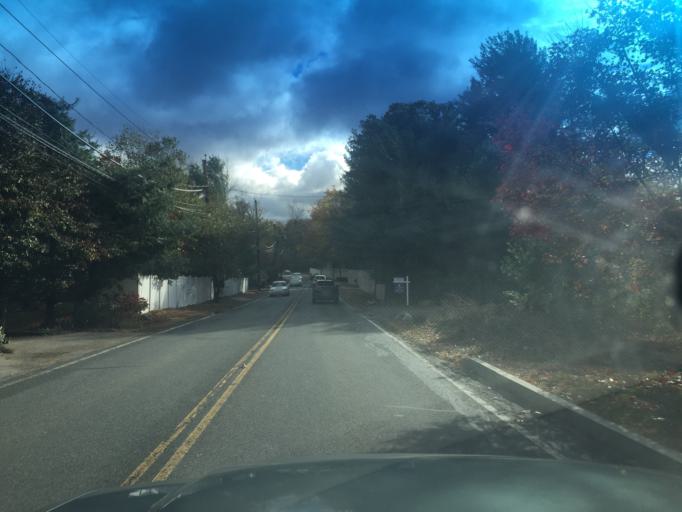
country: US
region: Massachusetts
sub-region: Norfolk County
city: Needham
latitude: 42.2665
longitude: -71.2155
